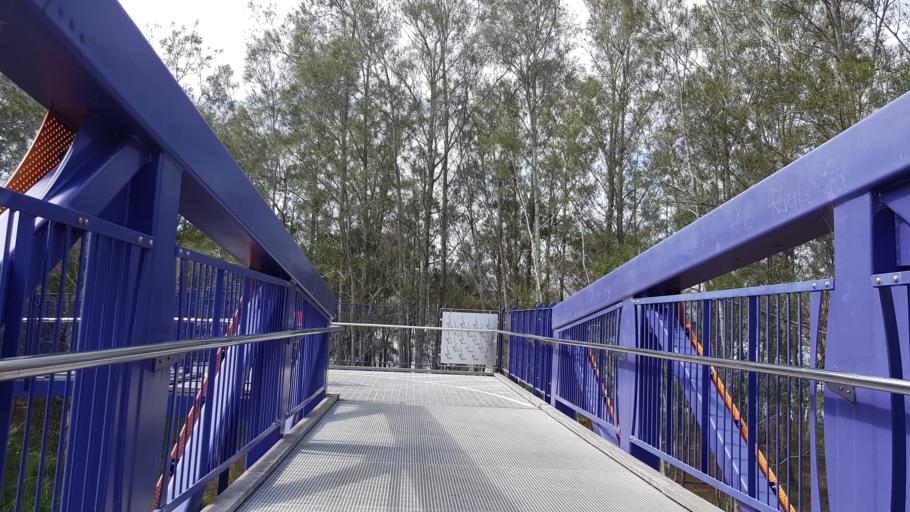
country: AU
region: New South Wales
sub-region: Pittwater
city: North Narrabeen
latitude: -33.7185
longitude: 151.2719
